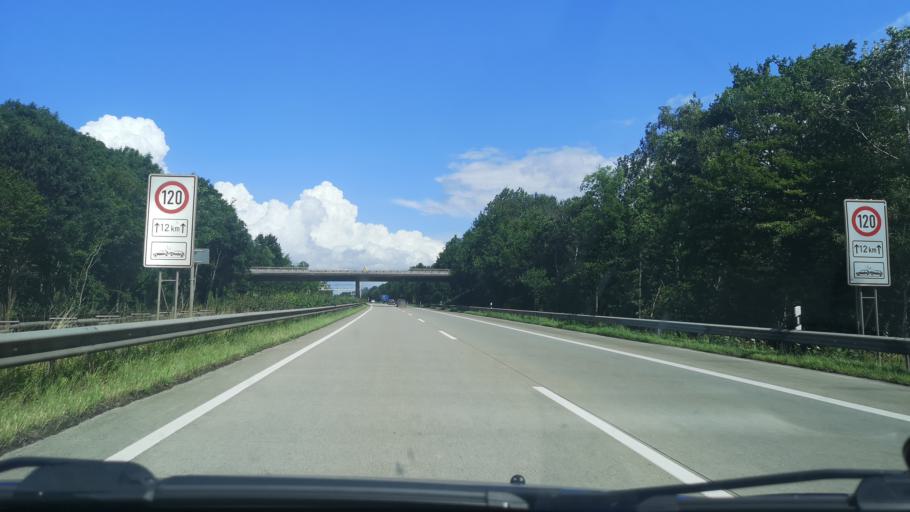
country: DE
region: Lower Saxony
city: Loxstedt
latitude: 53.4826
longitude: 8.6205
